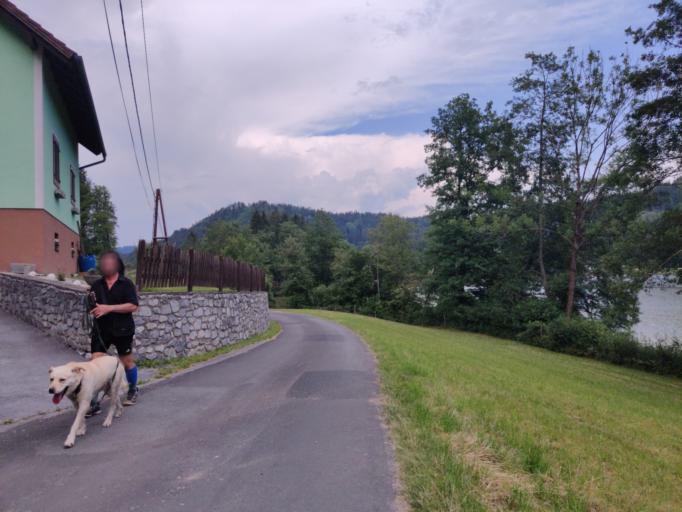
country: AT
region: Styria
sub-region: Politischer Bezirk Graz-Umgebung
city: Gratwein
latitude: 47.1122
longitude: 15.2953
